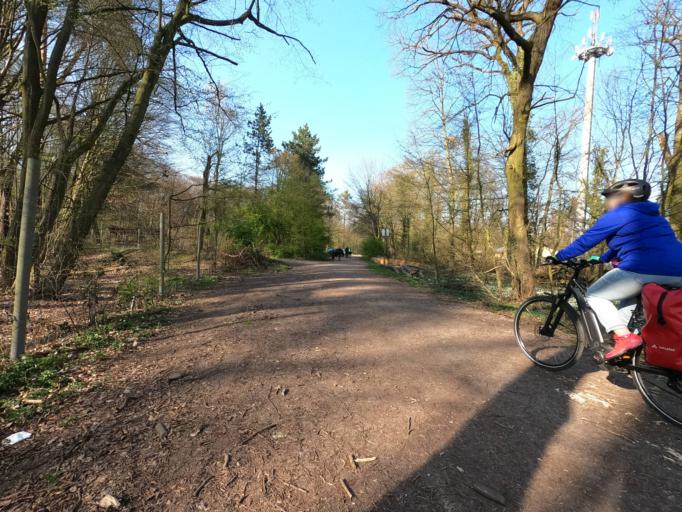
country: DE
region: Hesse
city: Morfelden-Walldorf
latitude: 49.9717
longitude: 8.5407
